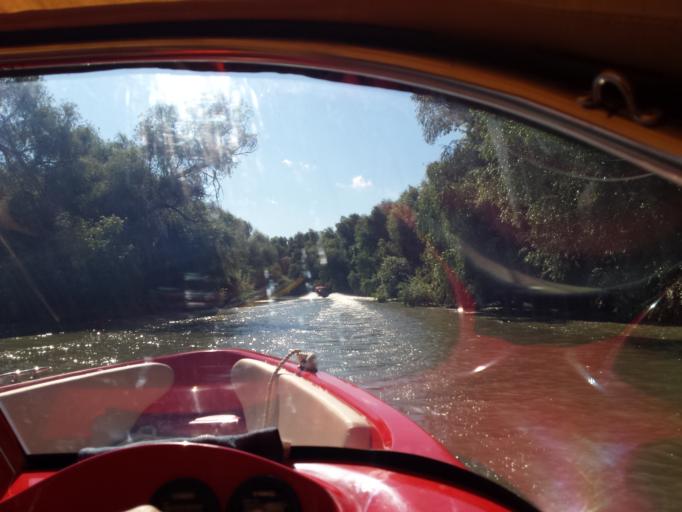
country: RO
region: Tulcea
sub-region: Comuna Pardina
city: Pardina
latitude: 45.2470
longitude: 29.0200
